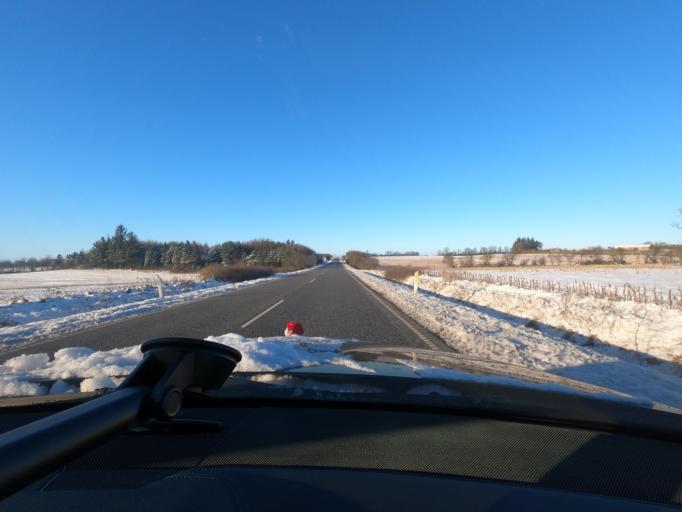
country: DK
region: South Denmark
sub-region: Tonder Kommune
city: Toftlund
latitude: 55.1166
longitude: 9.1628
